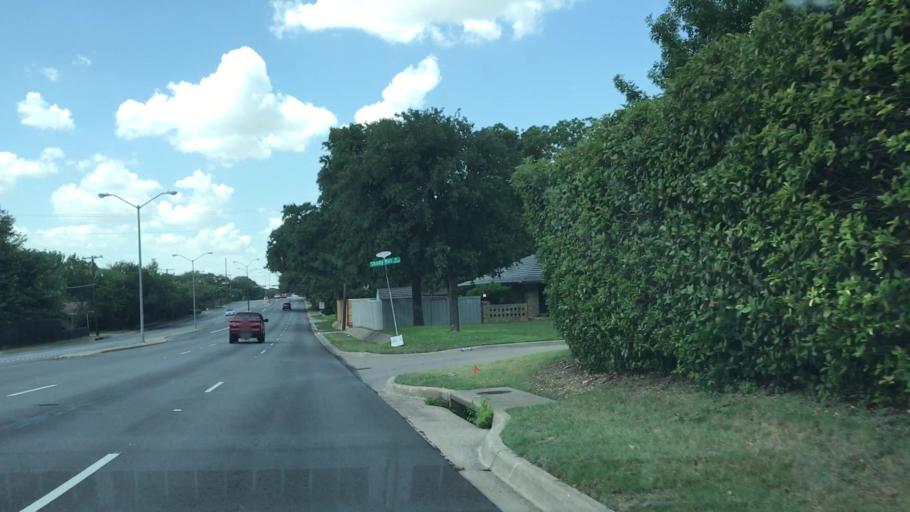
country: US
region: Texas
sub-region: Dallas County
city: Addison
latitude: 32.9058
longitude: -96.8382
